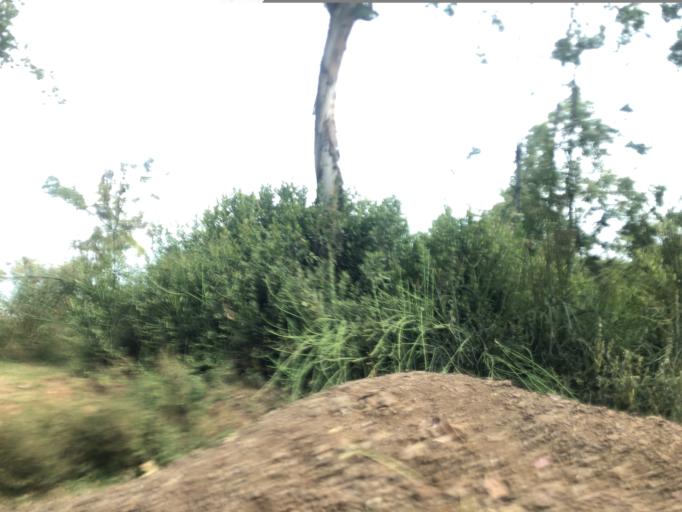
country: ET
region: Southern Nations, Nationalities, and People's Region
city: Konso
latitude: 5.2788
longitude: 37.3442
